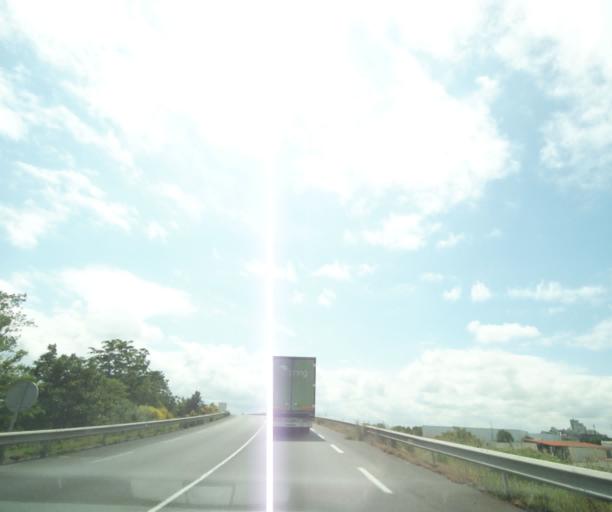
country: FR
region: Poitou-Charentes
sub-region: Departement des Deux-Sevres
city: Sainte-Verge
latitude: 47.0120
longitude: -0.1993
